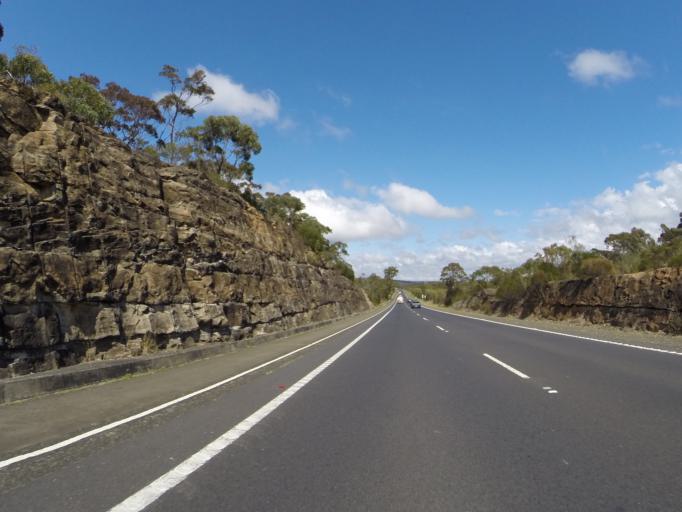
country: AU
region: New South Wales
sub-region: Wollongong
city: Helensburgh
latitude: -34.1807
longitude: 150.9742
